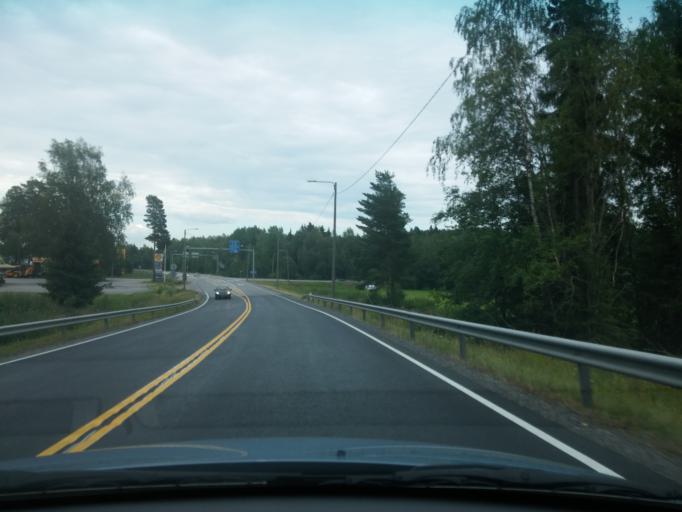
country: FI
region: Haeme
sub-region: Riihimaeki
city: Loppi
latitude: 60.7141
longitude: 24.4761
